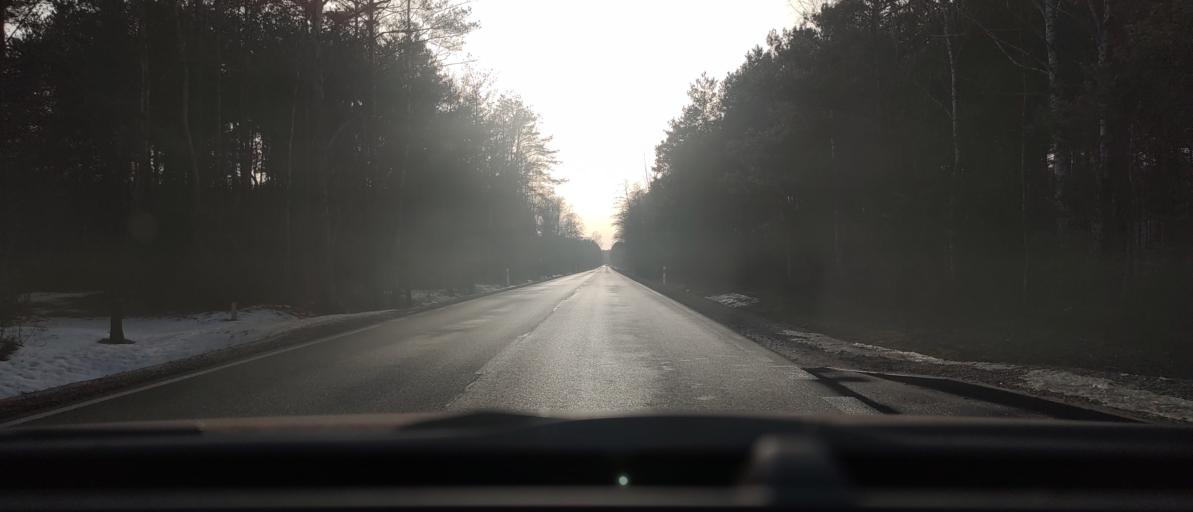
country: PL
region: Masovian Voivodeship
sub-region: Powiat bialobrzeski
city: Sucha
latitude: 51.6355
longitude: 20.9017
